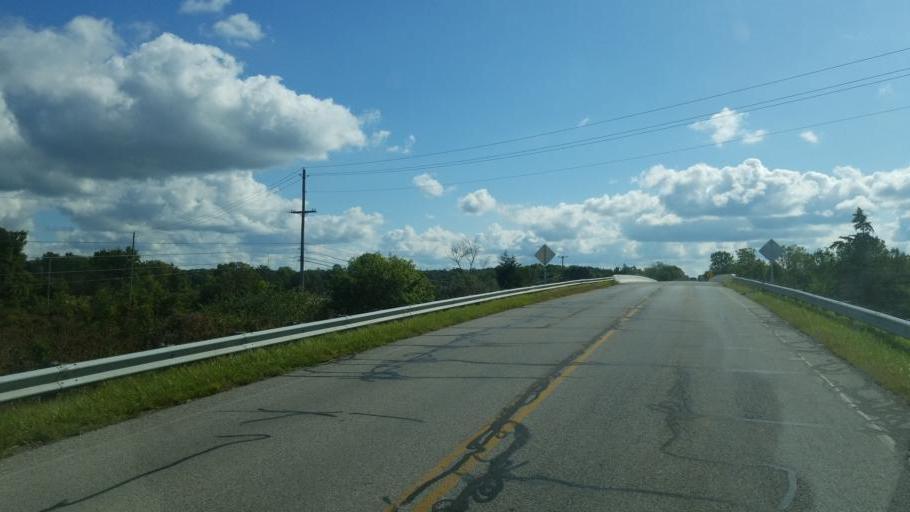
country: US
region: Ohio
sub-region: Lorain County
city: Oberlin
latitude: 41.2818
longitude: -82.1862
